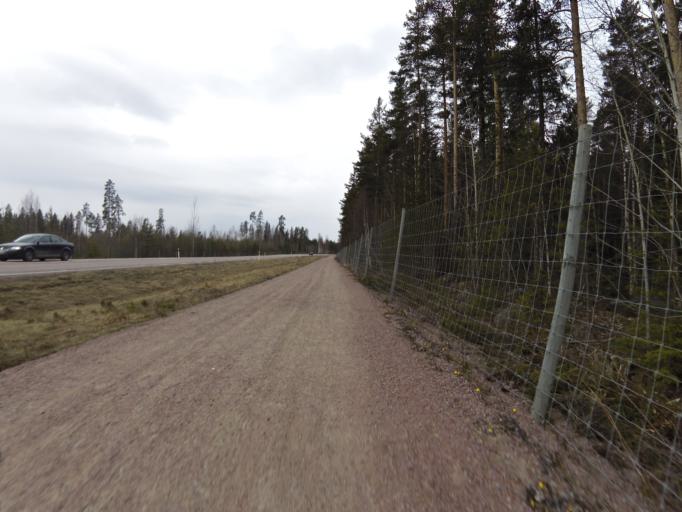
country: SE
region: Gaevleborg
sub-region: Hofors Kommun
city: Hofors
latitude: 60.5422
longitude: 16.2379
